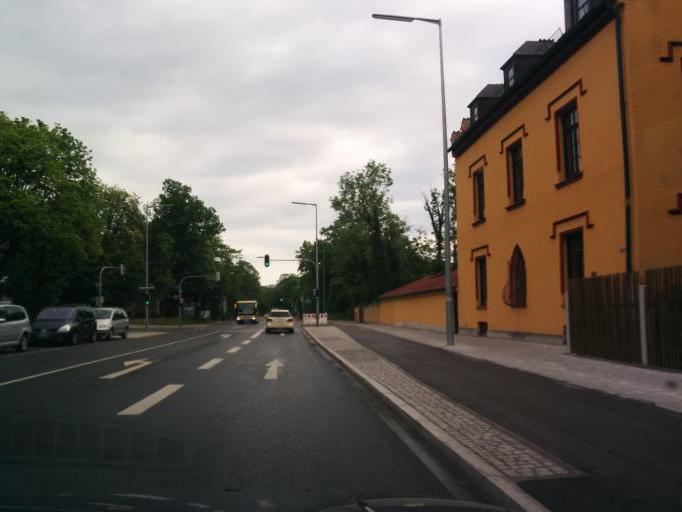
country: DE
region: Bavaria
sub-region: Upper Bavaria
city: Pullach im Isartal
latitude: 48.0959
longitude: 11.5411
